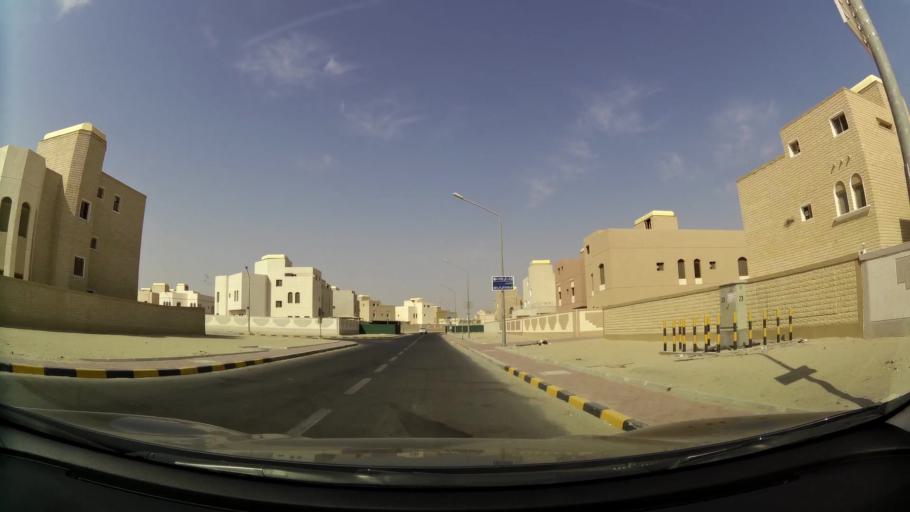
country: KW
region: Al Ahmadi
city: Al Wafrah
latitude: 28.7962
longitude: 48.0733
